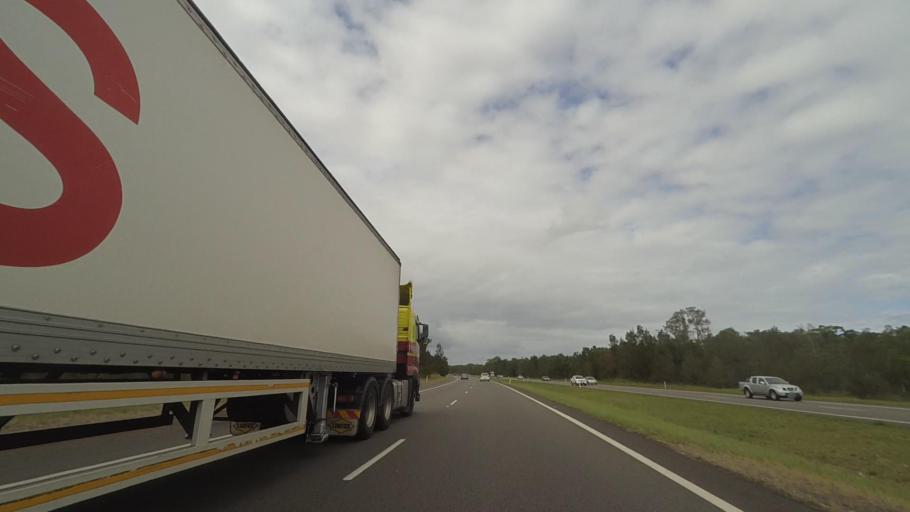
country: AU
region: New South Wales
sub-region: Port Stephens Shire
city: Raymond Terrace
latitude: -32.7761
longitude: 151.7553
